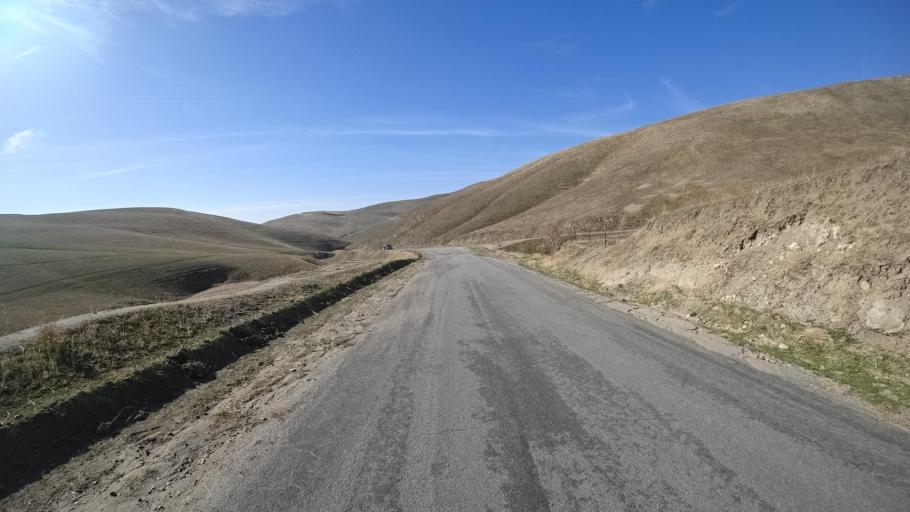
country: US
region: California
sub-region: Kern County
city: Arvin
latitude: 35.4097
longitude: -118.7647
